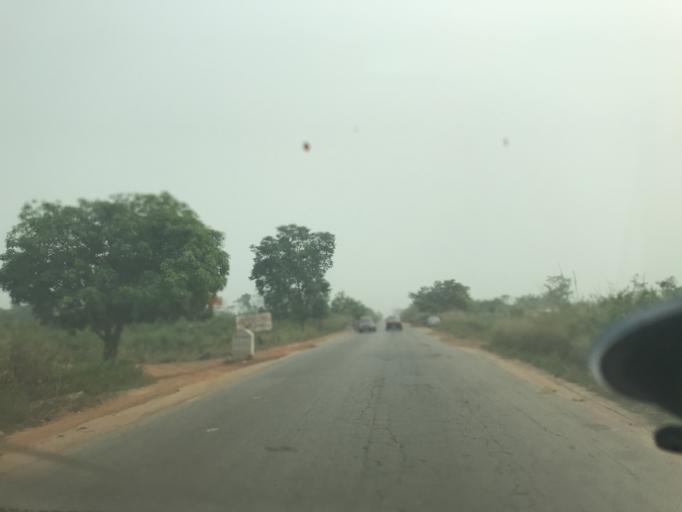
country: NG
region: Ogun
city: Ilaro
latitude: 6.8870
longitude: 3.0576
